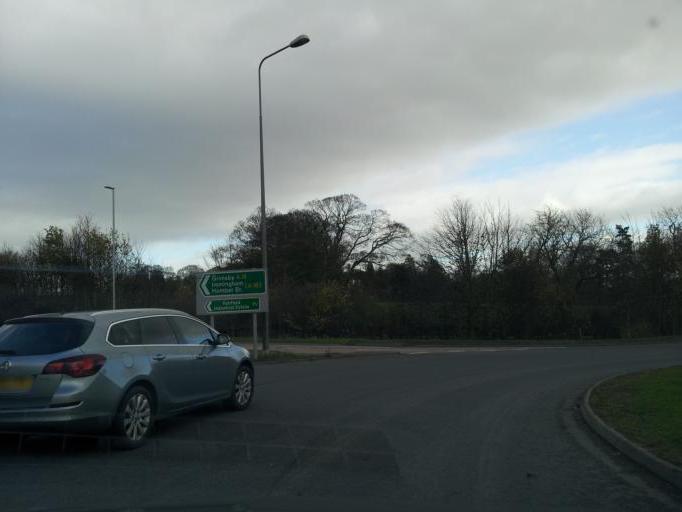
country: GB
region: England
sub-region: Lincolnshire
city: Louth
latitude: 53.3650
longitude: -0.0265
